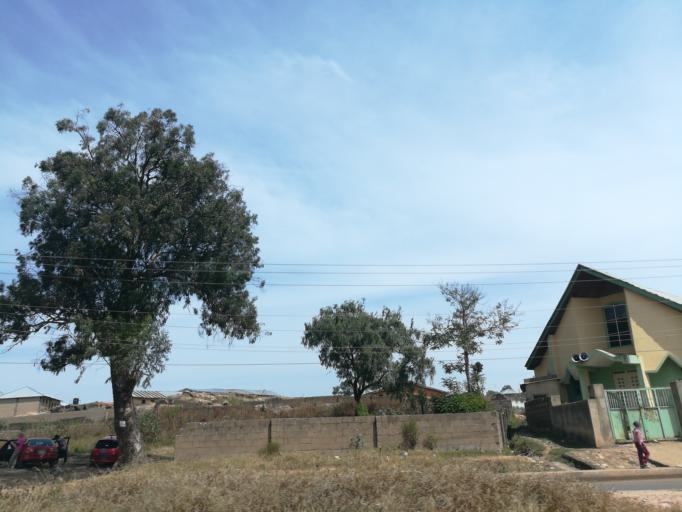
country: NG
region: Plateau
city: Bukuru
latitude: 9.7976
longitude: 8.8594
